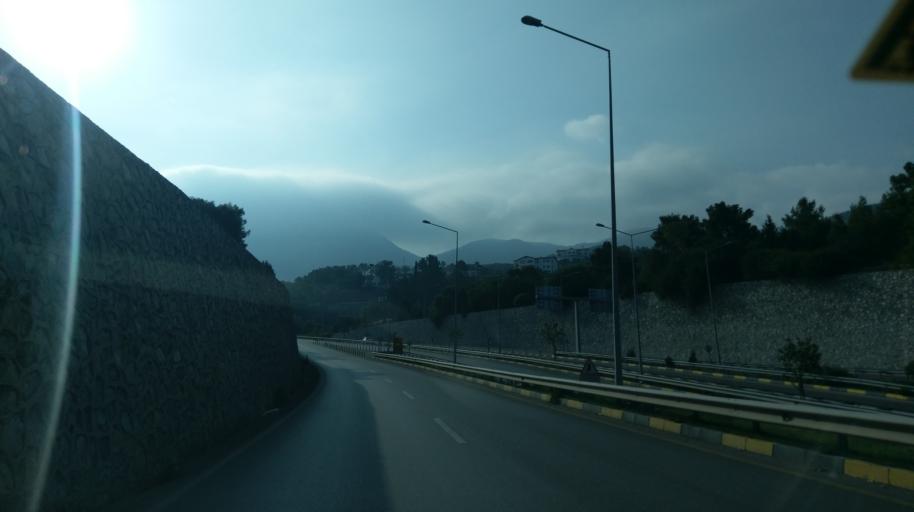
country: CY
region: Keryneia
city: Kyrenia
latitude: 35.3241
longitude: 33.3183
